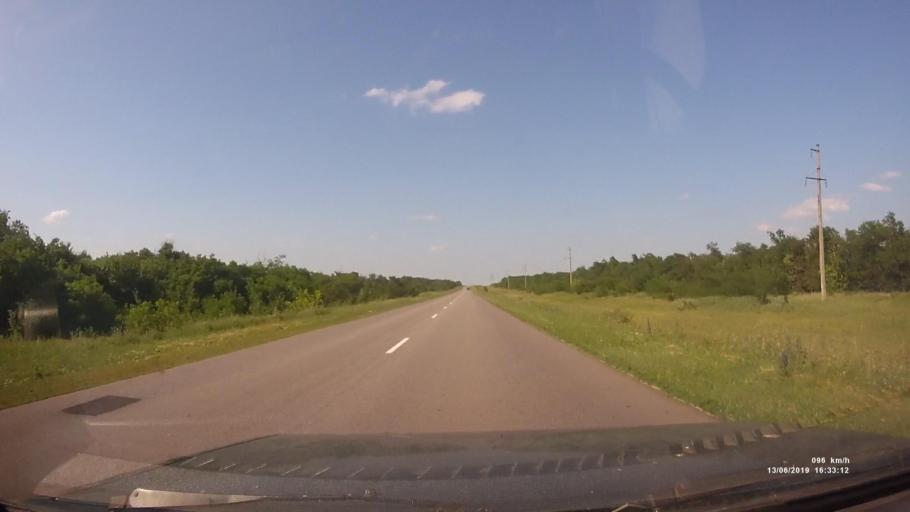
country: RU
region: Rostov
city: Kazanskaya
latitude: 49.8578
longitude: 41.2781
